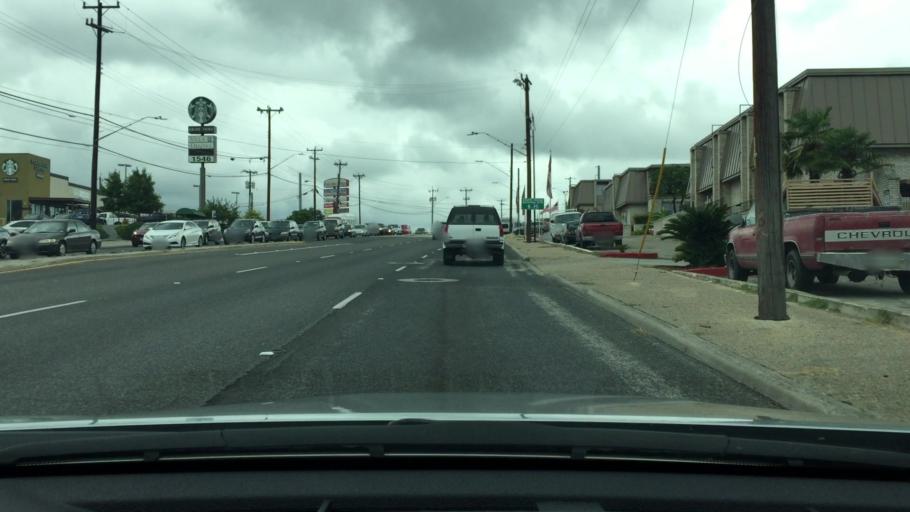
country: US
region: Texas
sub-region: Bexar County
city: Balcones Heights
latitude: 29.4906
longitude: -98.5685
